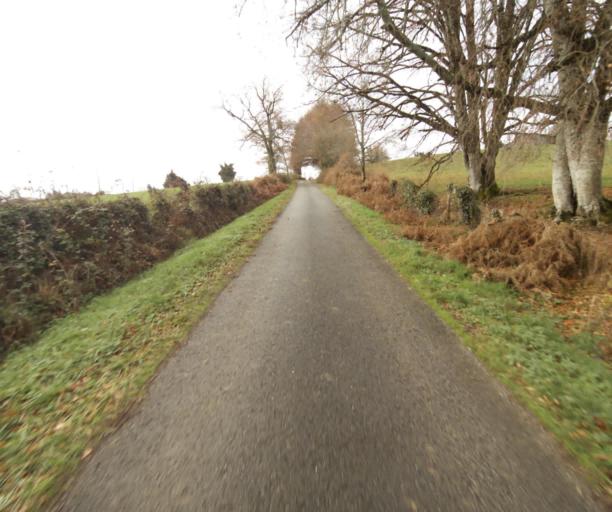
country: FR
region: Limousin
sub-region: Departement de la Correze
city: Sainte-Fereole
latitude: 45.2622
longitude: 1.6077
